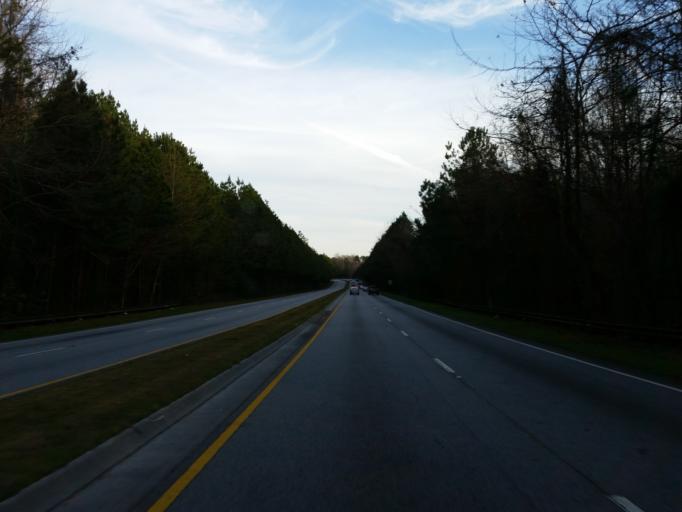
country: US
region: Georgia
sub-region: Cobb County
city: Mableton
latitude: 33.8488
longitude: -84.5526
